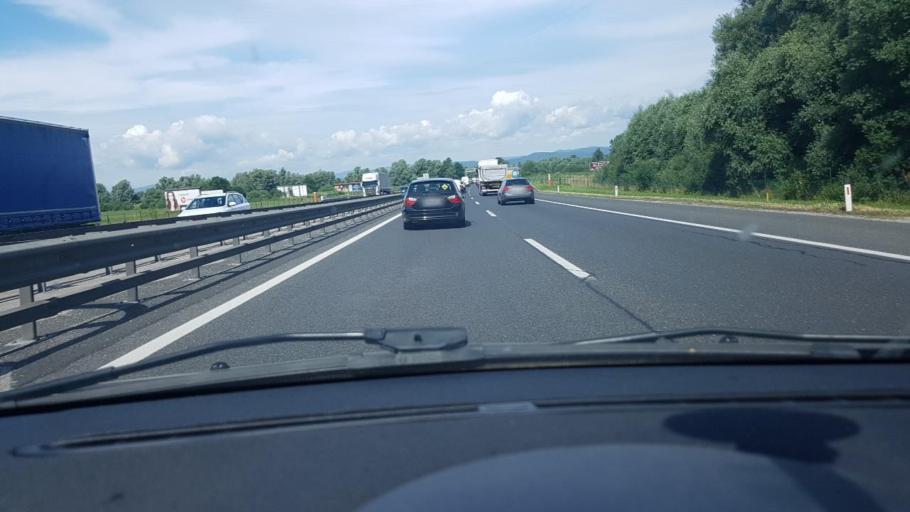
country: SI
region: Skofljica
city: Lavrica
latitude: 46.0137
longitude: 14.5371
